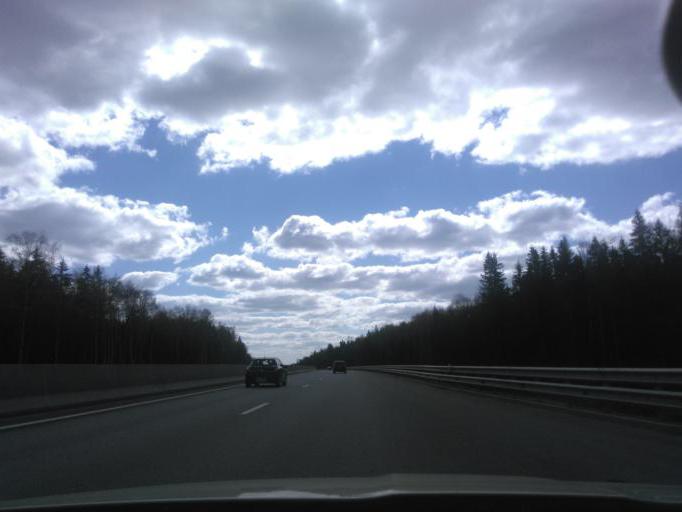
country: RU
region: Moskovskaya
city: Mendeleyevo
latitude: 56.0725
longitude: 37.2178
